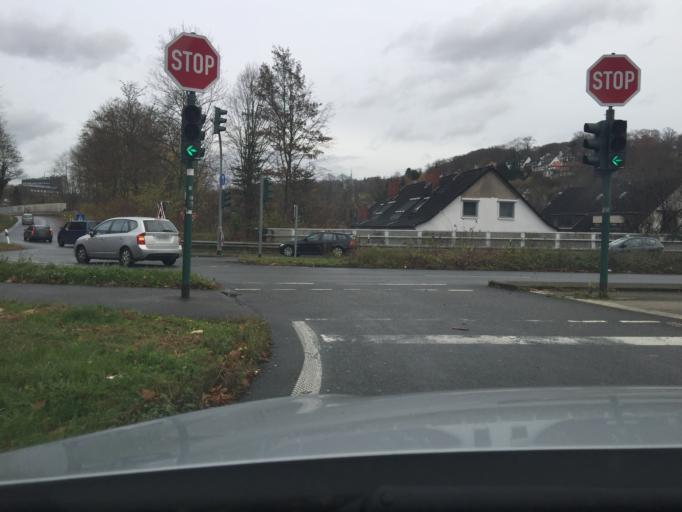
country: DE
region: North Rhine-Westphalia
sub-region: Regierungsbezirk Dusseldorf
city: Velbert
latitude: 51.3859
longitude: 7.0816
